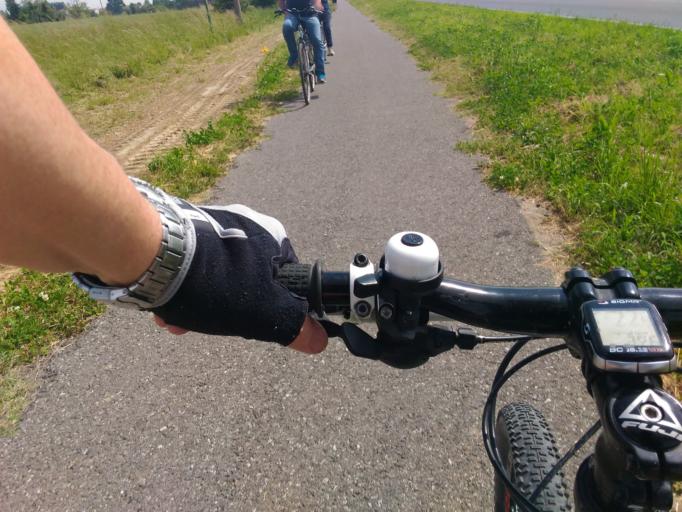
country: IT
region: Lombardy
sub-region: Provincia di Lodi
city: Mulazzano
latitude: 45.3700
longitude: 9.3824
